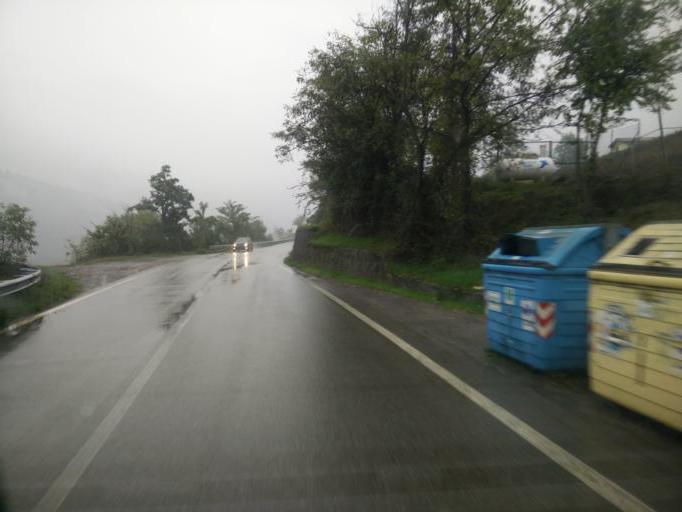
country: IT
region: Emilia-Romagna
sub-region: Provincia di Bologna
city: Vado
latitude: 44.2912
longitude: 11.2251
